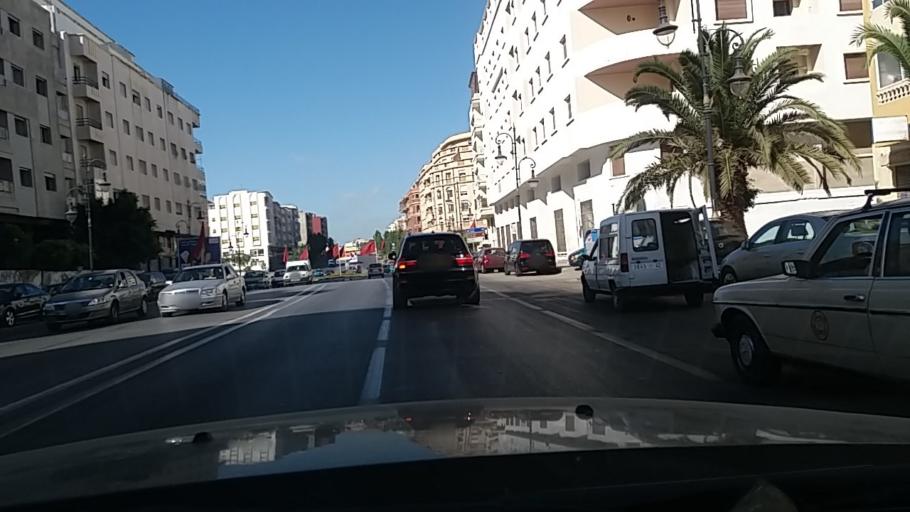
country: MA
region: Tanger-Tetouan
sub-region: Tanger-Assilah
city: Tangier
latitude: 35.7636
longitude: -5.8376
